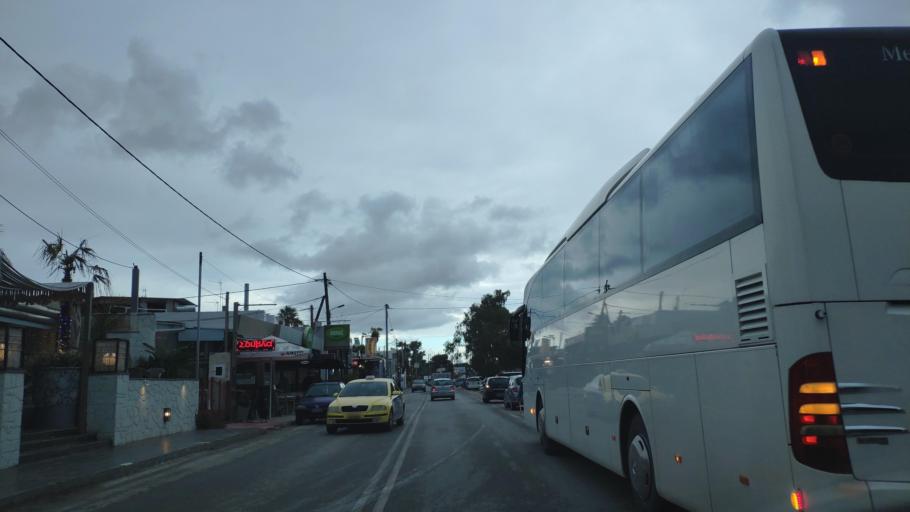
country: GR
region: Attica
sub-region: Nomarchia Anatolikis Attikis
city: Artemida
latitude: 37.9815
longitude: 24.0095
